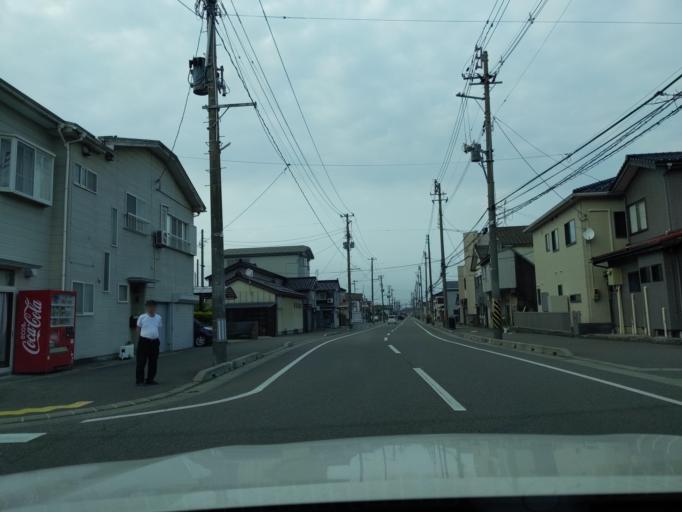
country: JP
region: Niigata
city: Kashiwazaki
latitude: 37.3768
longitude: 138.5627
